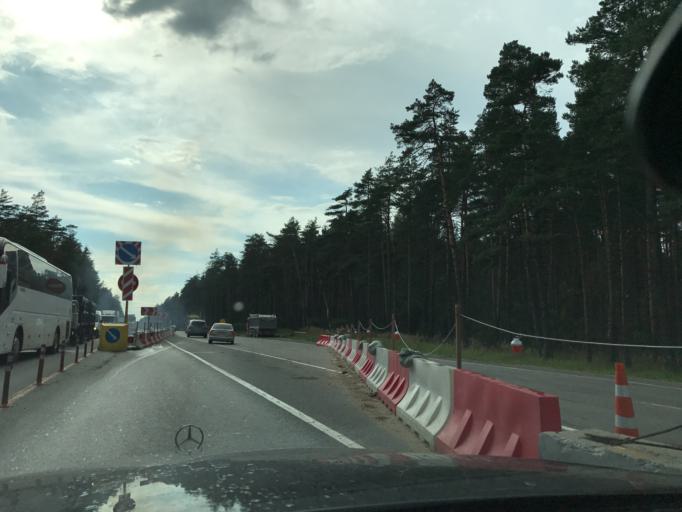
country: RU
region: Moskovskaya
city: Malaya Dubna
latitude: 55.8826
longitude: 38.9914
